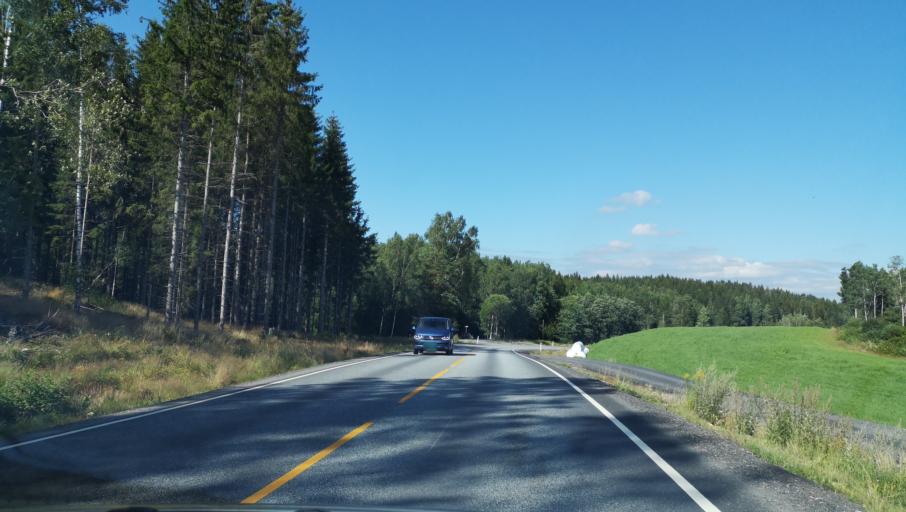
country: NO
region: Ostfold
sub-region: Hobol
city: Elvestad
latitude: 59.5847
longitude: 10.8762
